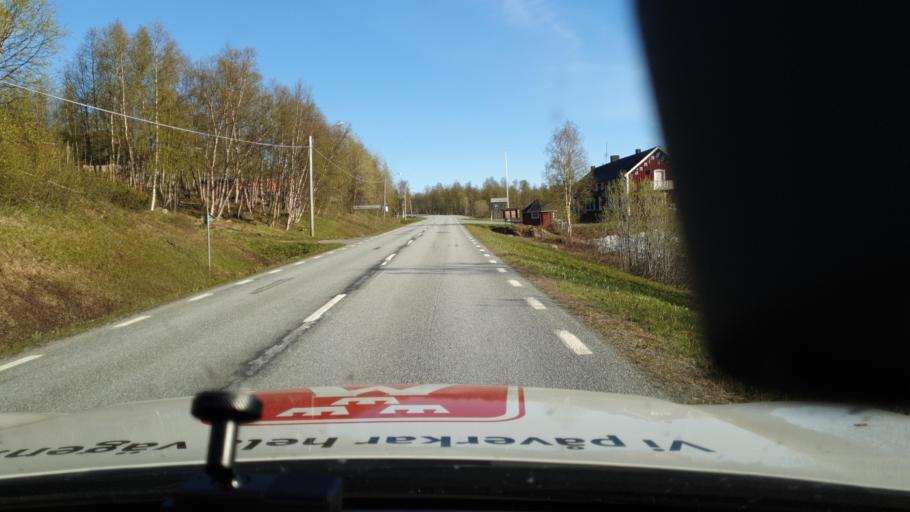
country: NO
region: Nordland
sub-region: Rana
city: Mo i Rana
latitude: 65.8693
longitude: 15.0145
